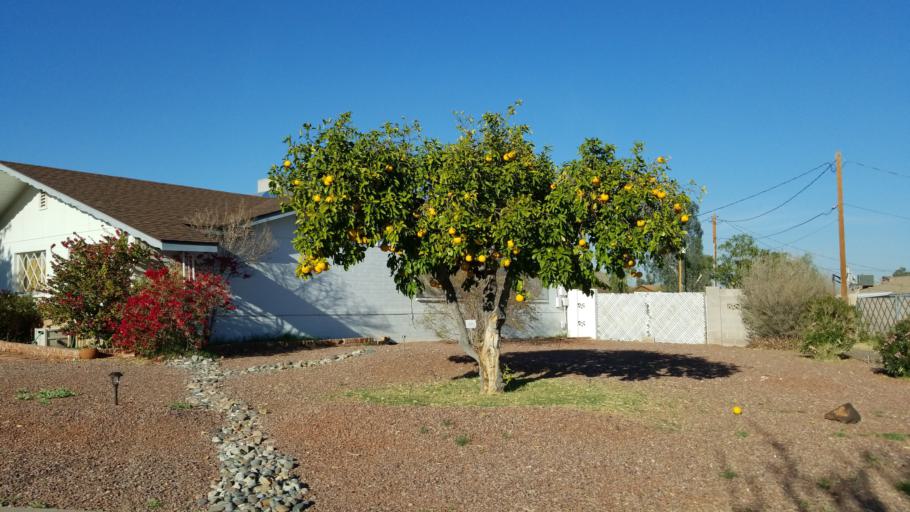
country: US
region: Arizona
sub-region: Maricopa County
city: Paradise Valley
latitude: 33.5994
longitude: -112.0358
